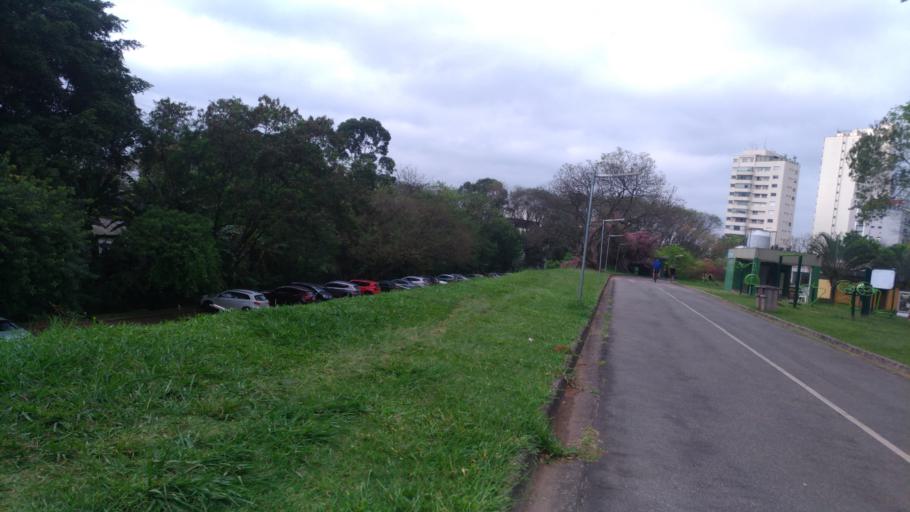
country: BR
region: Sao Paulo
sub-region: Osasco
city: Osasco
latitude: -23.5476
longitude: -46.7180
